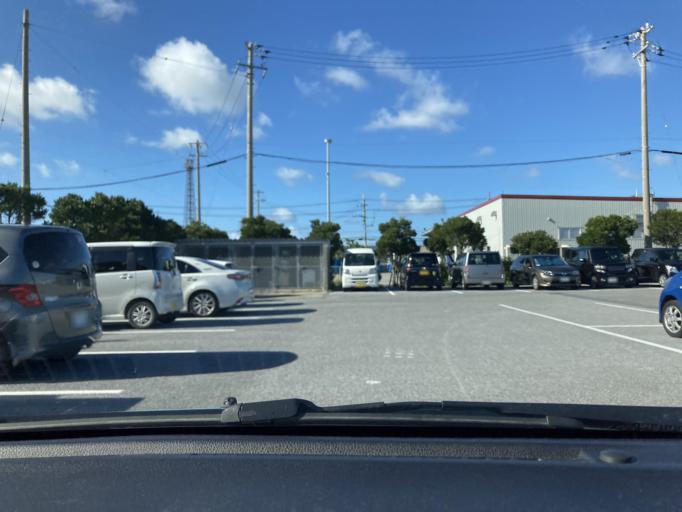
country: JP
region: Okinawa
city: Itoman
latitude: 26.1383
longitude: 127.6606
